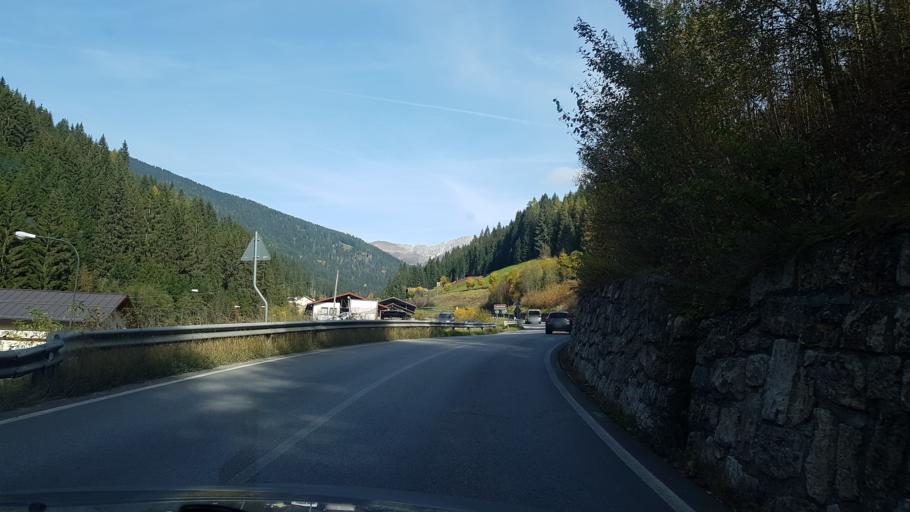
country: IT
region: Veneto
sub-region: Provincia di Belluno
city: San Nicolo Comelico
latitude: 46.5843
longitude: 12.5228
